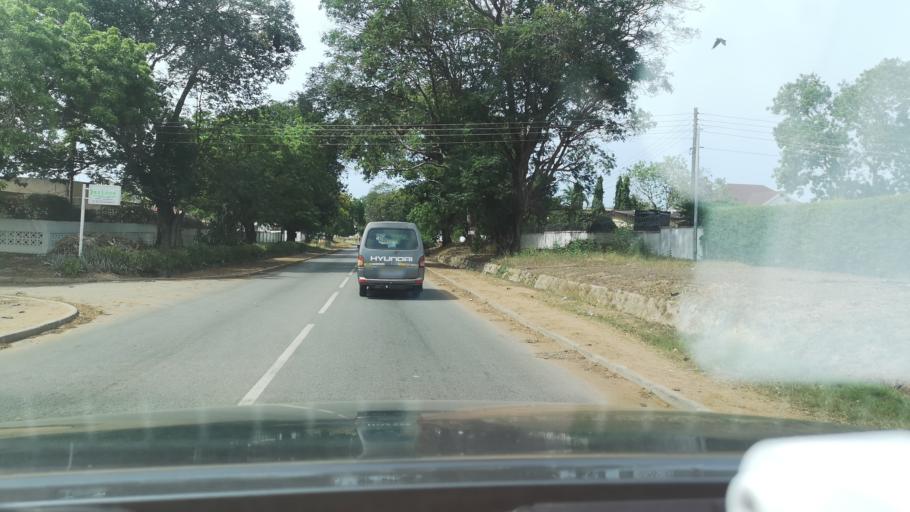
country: GH
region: Greater Accra
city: Tema
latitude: 5.6565
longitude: -0.0222
